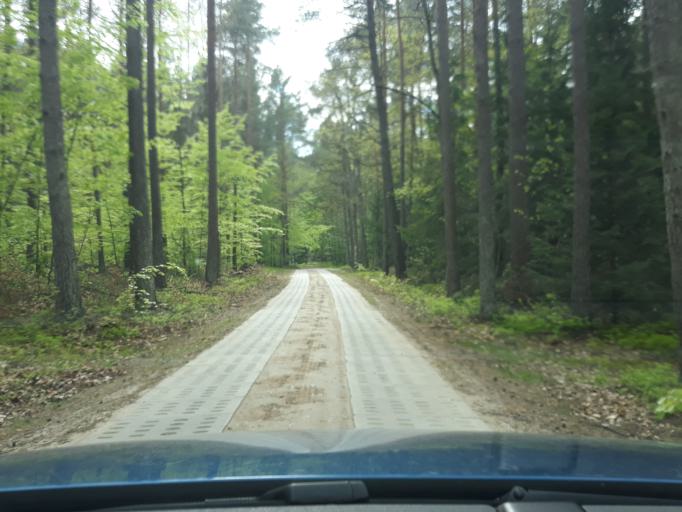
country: PL
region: Pomeranian Voivodeship
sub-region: Powiat czluchowski
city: Czluchow
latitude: 53.7425
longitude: 17.3471
